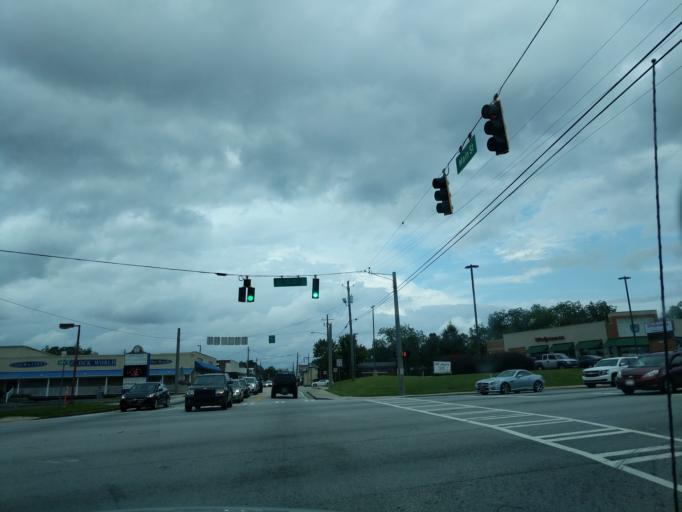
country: US
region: Georgia
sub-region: Walton County
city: Loganville
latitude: 33.8382
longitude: -83.9023
